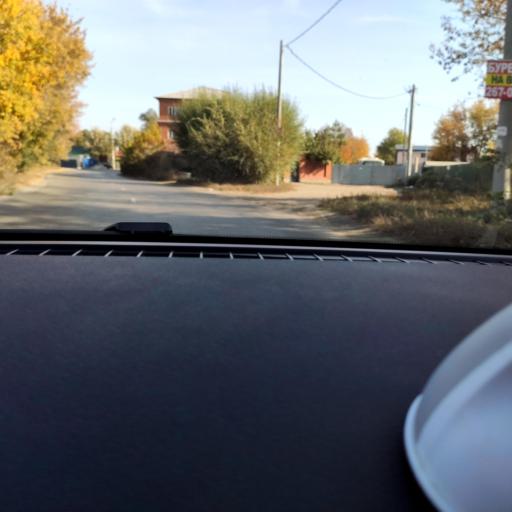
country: RU
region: Samara
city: Smyshlyayevka
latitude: 53.2348
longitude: 50.3201
